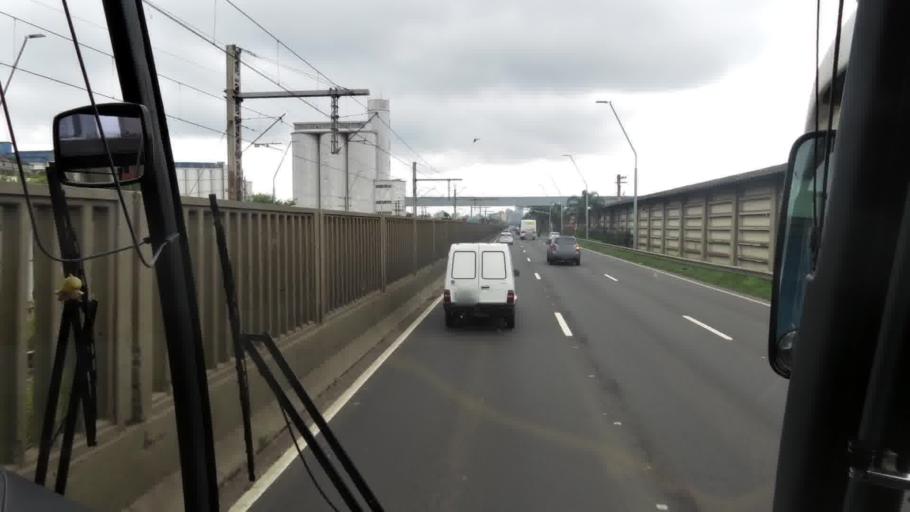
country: BR
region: Rio Grande do Sul
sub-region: Porto Alegre
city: Porto Alegre
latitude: -30.0081
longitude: -51.2104
